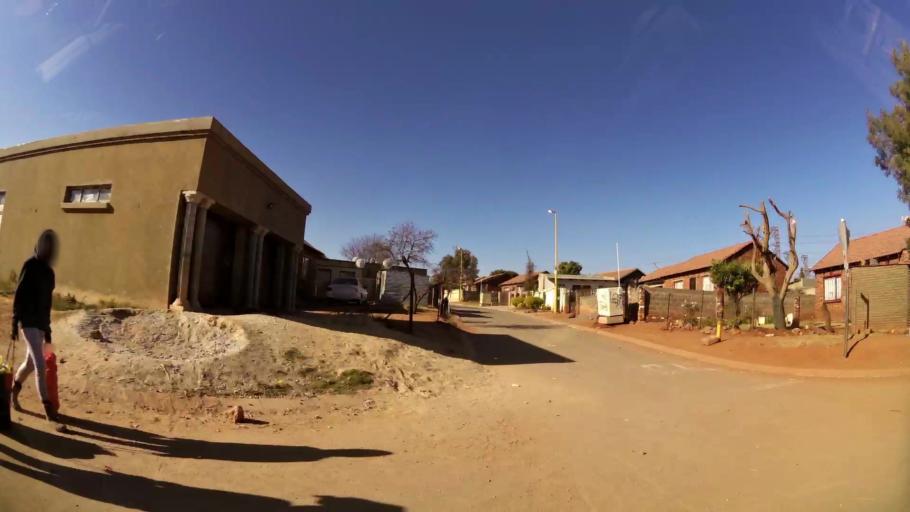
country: ZA
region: Gauteng
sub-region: Ekurhuleni Metropolitan Municipality
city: Tembisa
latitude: -26.0298
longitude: 28.2201
